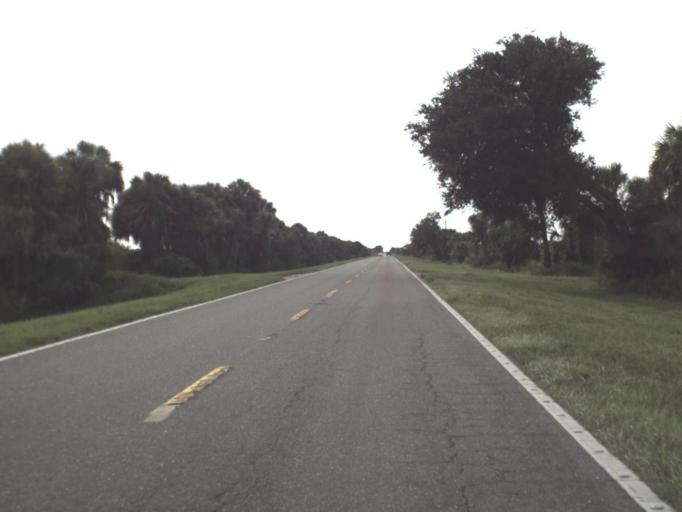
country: US
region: Florida
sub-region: Hendry County
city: Port LaBelle
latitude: 26.7685
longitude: -81.2864
